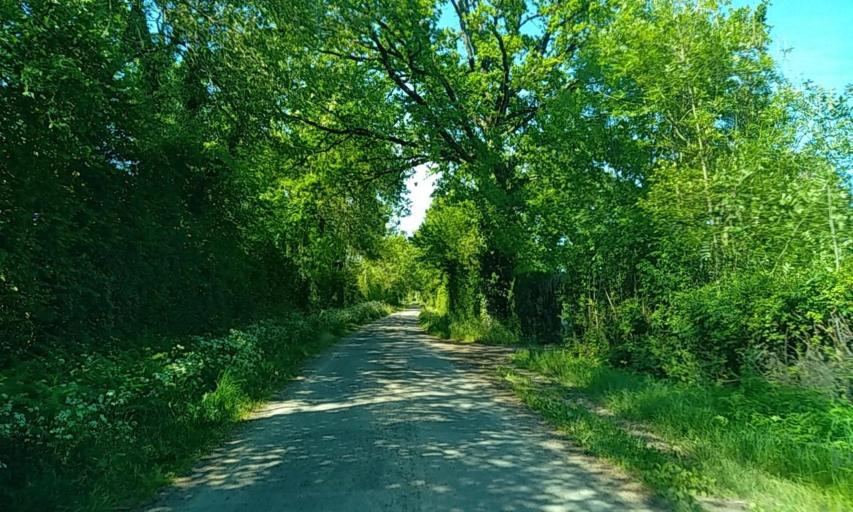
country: FR
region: Poitou-Charentes
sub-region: Departement des Deux-Sevres
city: Boisme
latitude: 46.7956
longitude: -0.4644
